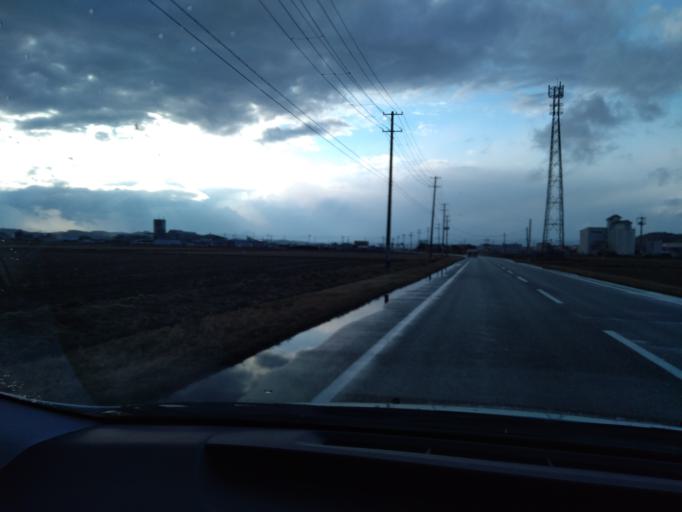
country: JP
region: Iwate
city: Ichinoseki
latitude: 38.8003
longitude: 141.0737
